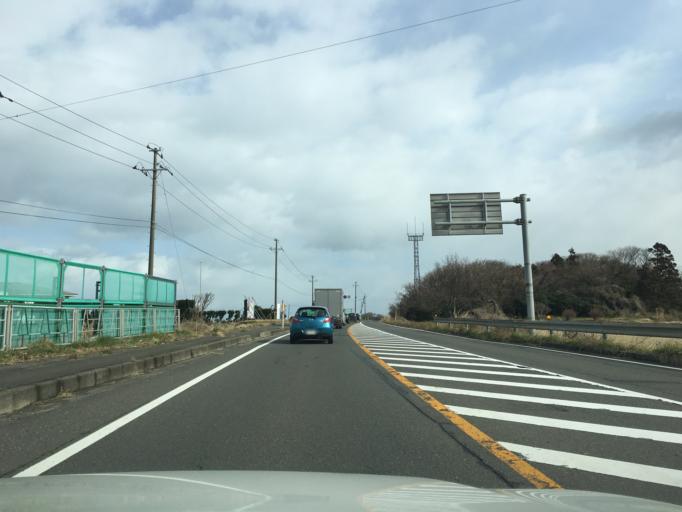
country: JP
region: Yamagata
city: Yuza
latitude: 39.2730
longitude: 139.9241
